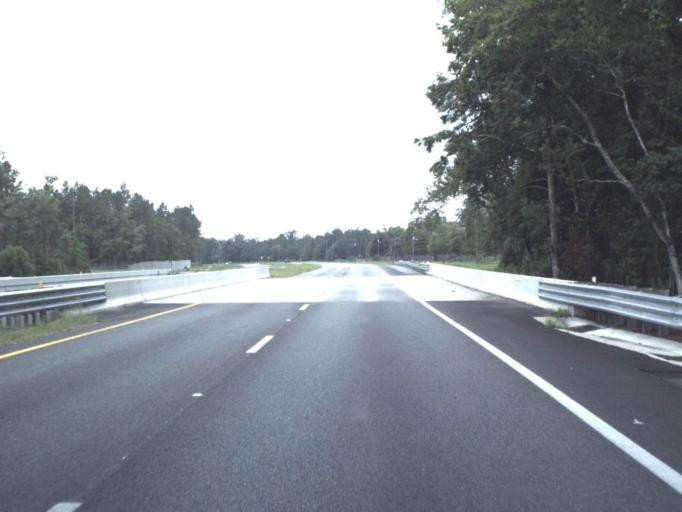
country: US
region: Florida
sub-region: Nassau County
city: Nassau Village-Ratliff
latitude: 30.4767
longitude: -81.9043
